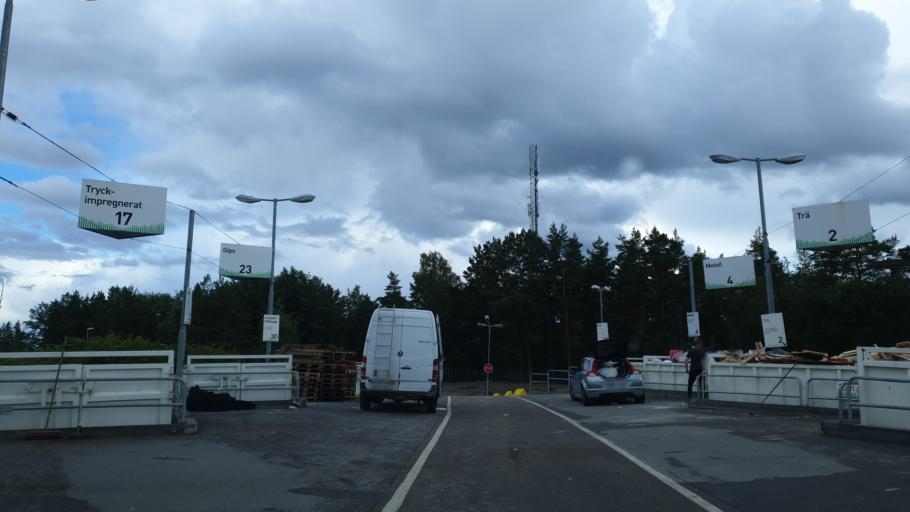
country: SE
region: Stockholm
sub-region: Jarfalla Kommun
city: Jakobsberg
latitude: 59.4284
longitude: 17.8030
